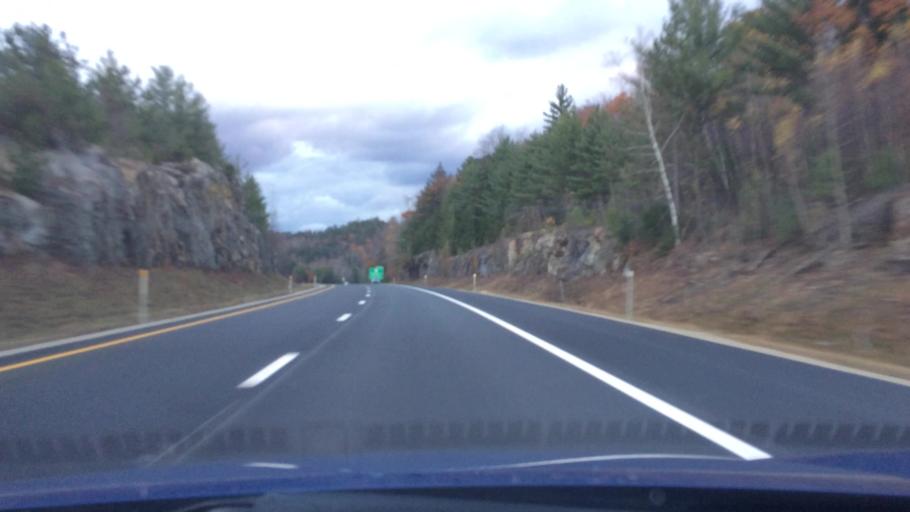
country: US
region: New Hampshire
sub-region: Grafton County
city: Woodstock
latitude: 43.9410
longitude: -71.6873
